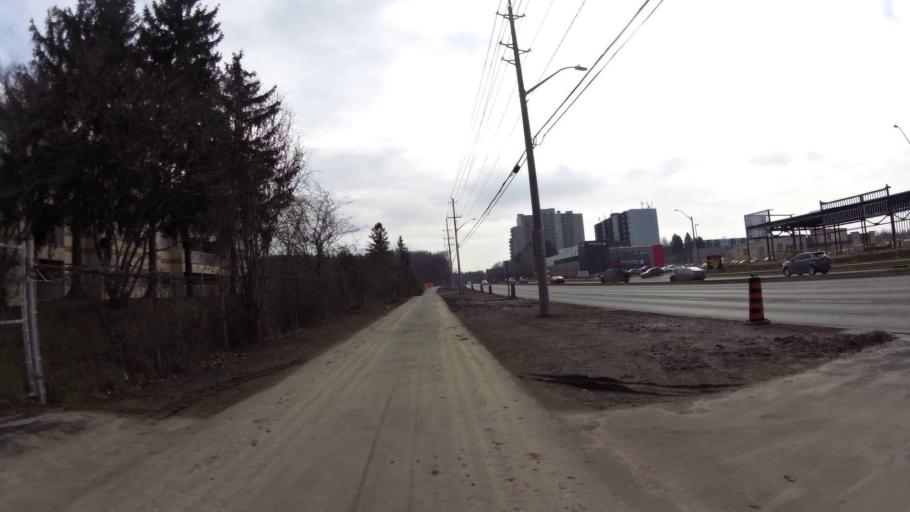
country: CA
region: Ontario
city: Kitchener
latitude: 43.3949
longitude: -80.4311
